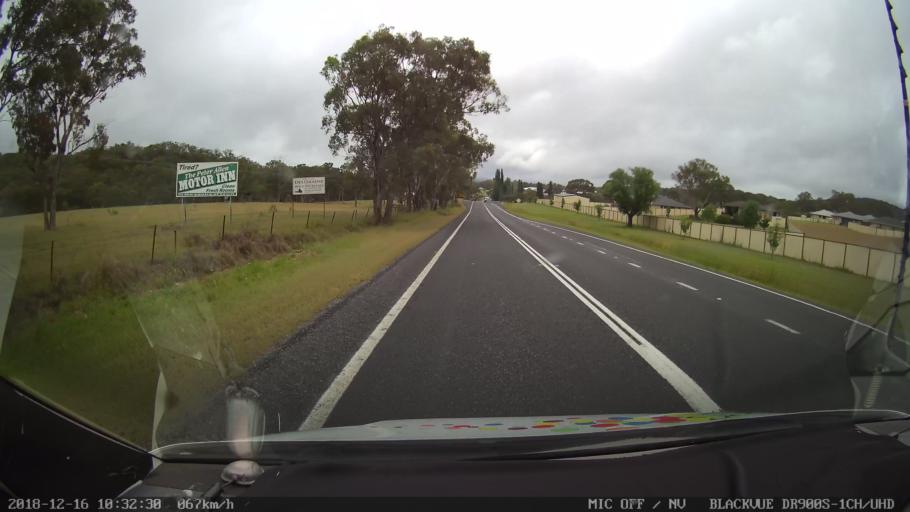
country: AU
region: New South Wales
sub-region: Tenterfield Municipality
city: Carrolls Creek
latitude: -29.0720
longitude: 152.0118
